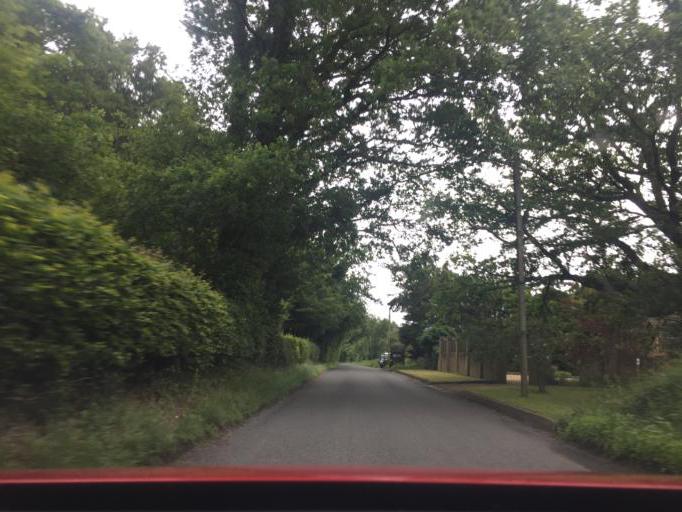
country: GB
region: England
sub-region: Hertfordshire
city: Harpenden
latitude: 51.8548
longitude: -0.3303
